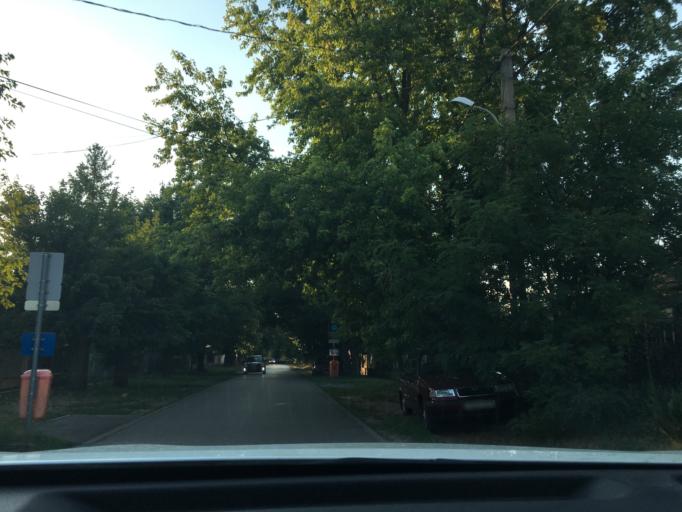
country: HU
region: Budapest
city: Budapest XVII. keruelet
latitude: 47.4786
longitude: 19.2786
